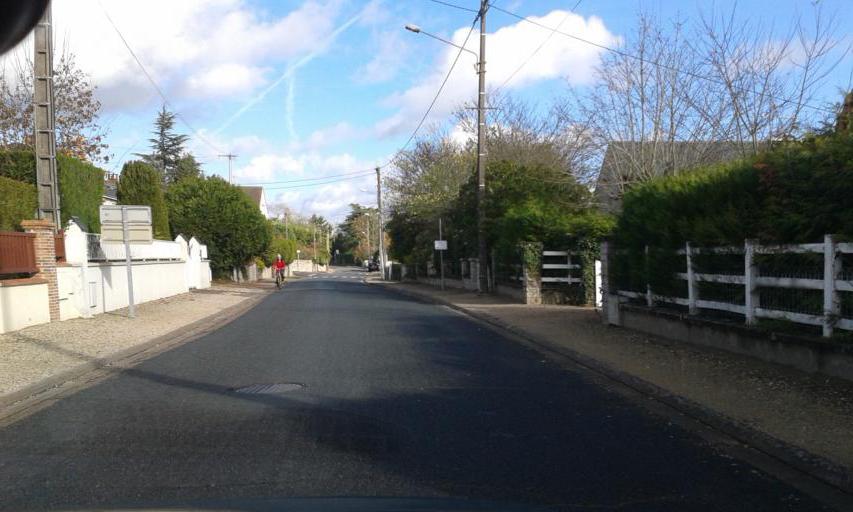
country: FR
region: Centre
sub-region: Departement du Loiret
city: Beaugency
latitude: 47.7661
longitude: 1.6261
